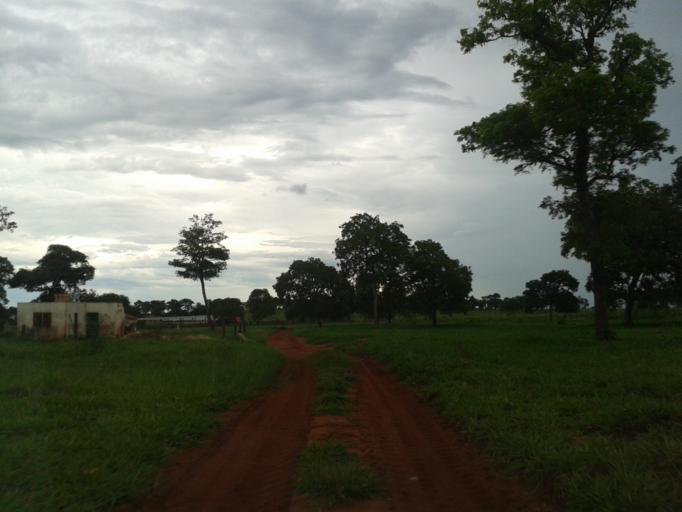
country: BR
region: Minas Gerais
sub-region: Santa Vitoria
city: Santa Vitoria
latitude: -19.2013
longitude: -50.5152
